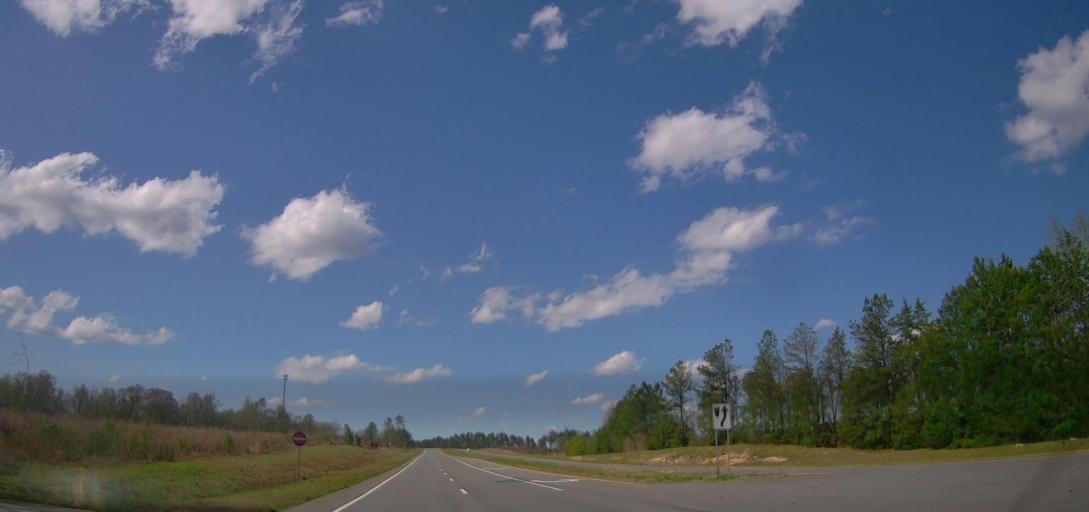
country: US
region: Georgia
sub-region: Baldwin County
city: Hardwick
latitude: 32.9871
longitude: -83.2124
